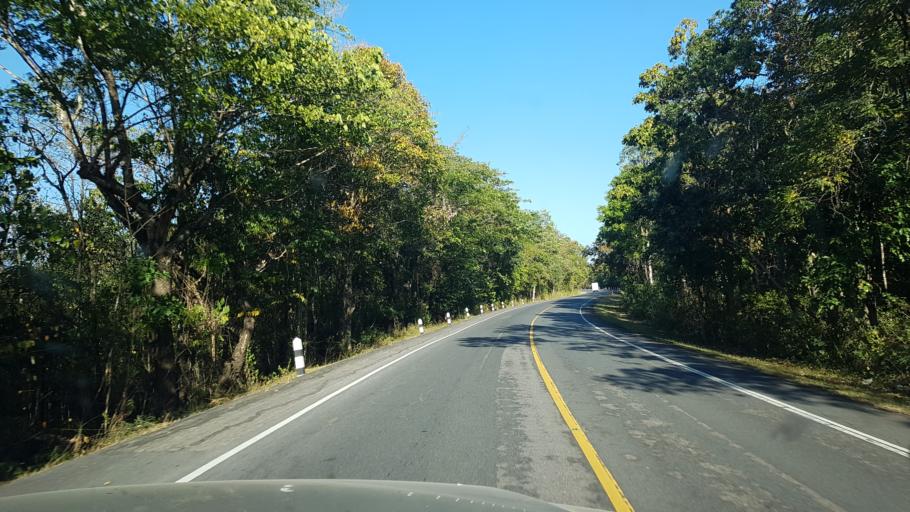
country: TH
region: Phetchabun
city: Nam Nao
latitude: 16.7517
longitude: 101.4554
